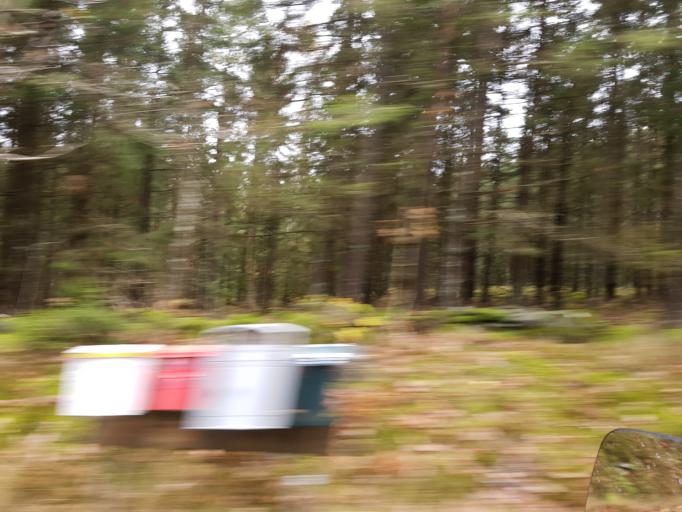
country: SE
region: Vaestra Goetaland
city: Svanesund
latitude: 58.1751
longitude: 11.7630
